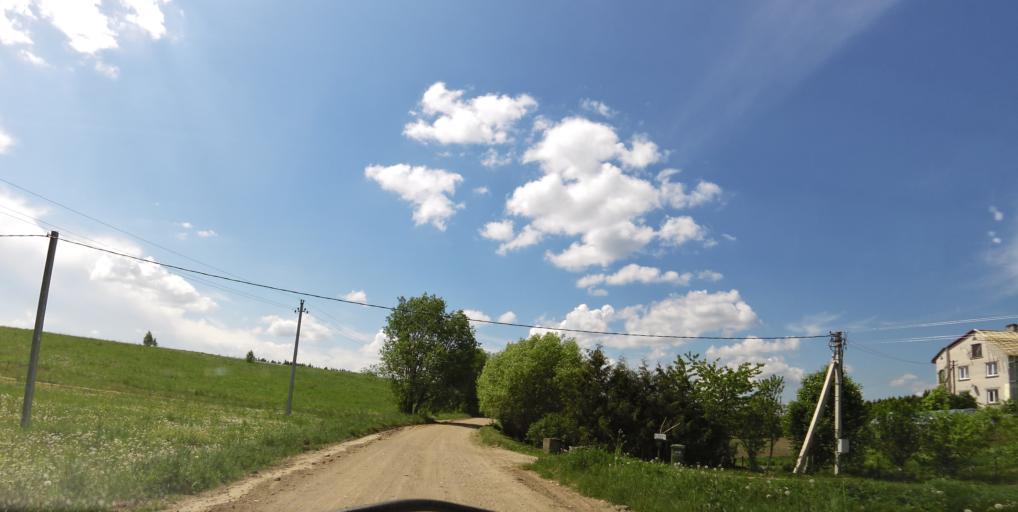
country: LT
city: Grigiskes
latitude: 54.7471
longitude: 25.1215
